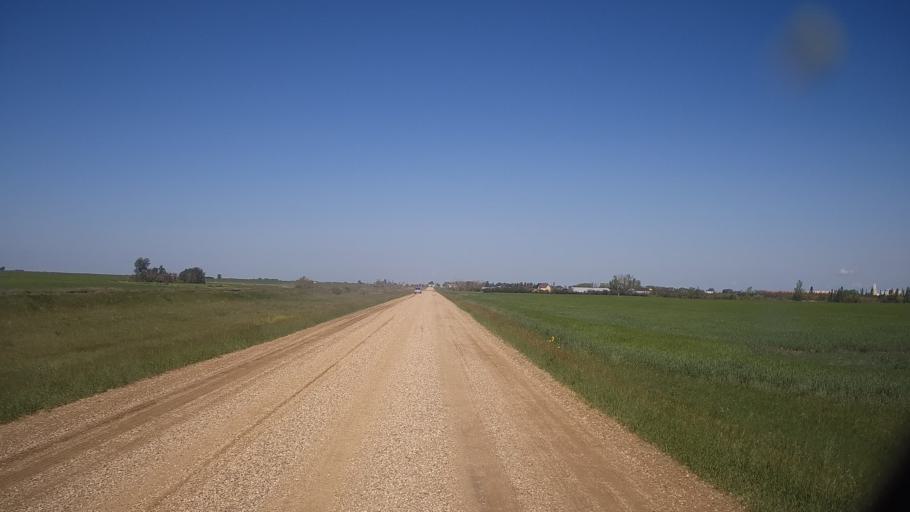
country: CA
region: Saskatchewan
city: Watrous
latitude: 51.8829
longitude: -106.0278
